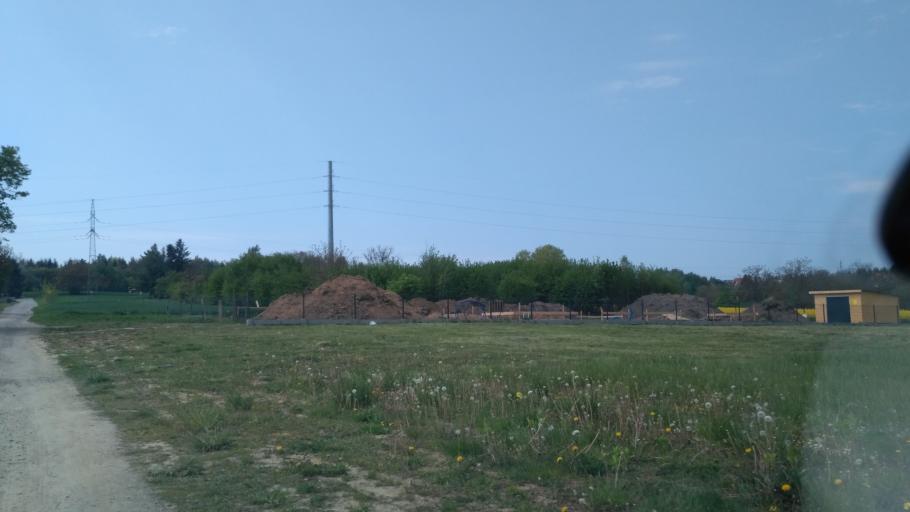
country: PL
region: Subcarpathian Voivodeship
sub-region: Powiat jaroslawski
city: Jaroslaw
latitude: 49.9993
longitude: 22.6794
